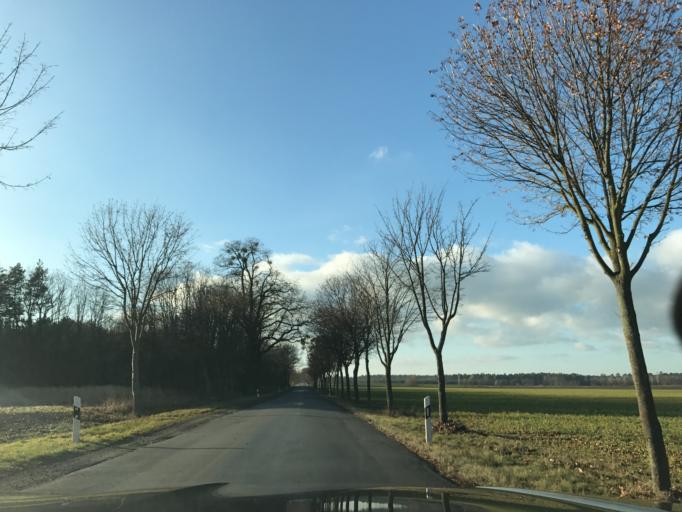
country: DE
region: Saxony-Anhalt
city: Loburg
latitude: 52.1713
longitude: 12.0320
